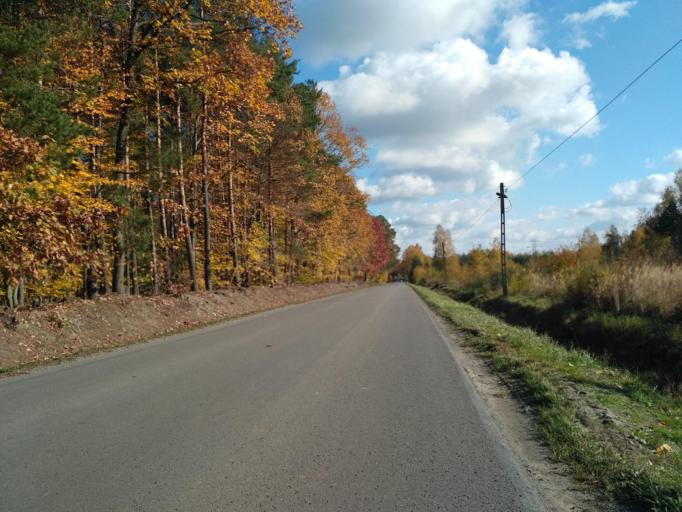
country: PL
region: Subcarpathian Voivodeship
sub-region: Powiat rzeszowski
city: Glogow Malopolski
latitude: 50.1552
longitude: 21.9269
